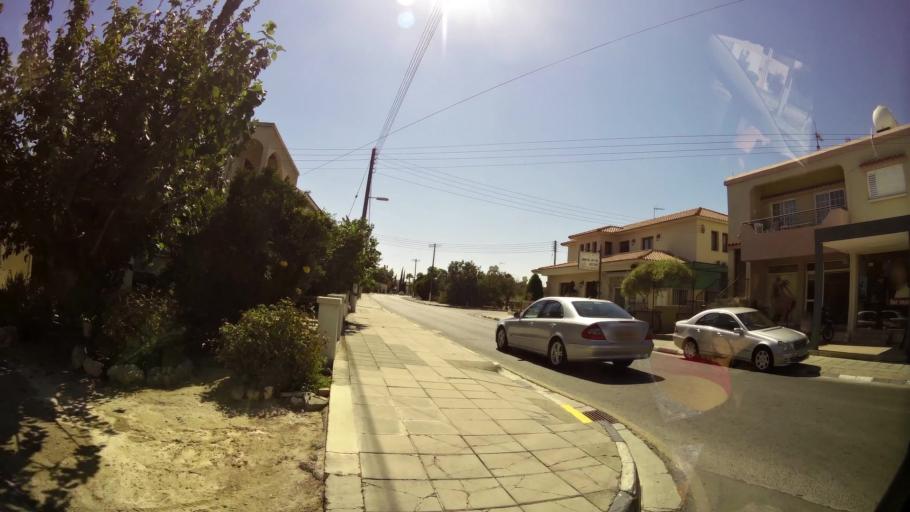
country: CY
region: Larnaka
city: Livadia
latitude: 34.9536
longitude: 33.6260
